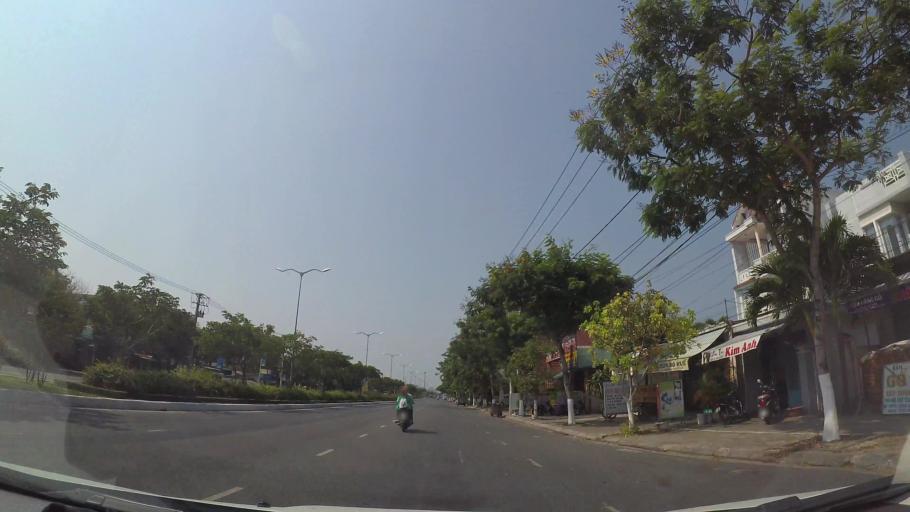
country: VN
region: Da Nang
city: Ngu Hanh Son
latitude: 16.0070
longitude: 108.2590
